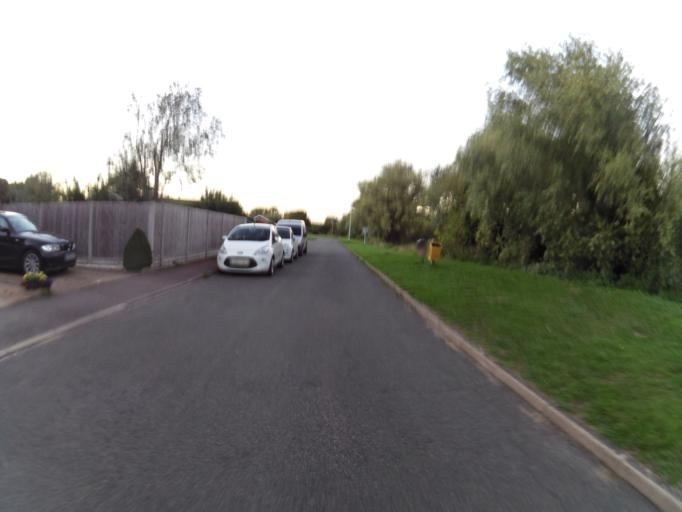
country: GB
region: England
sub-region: Suffolk
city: Bramford
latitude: 52.0771
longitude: 1.1014
